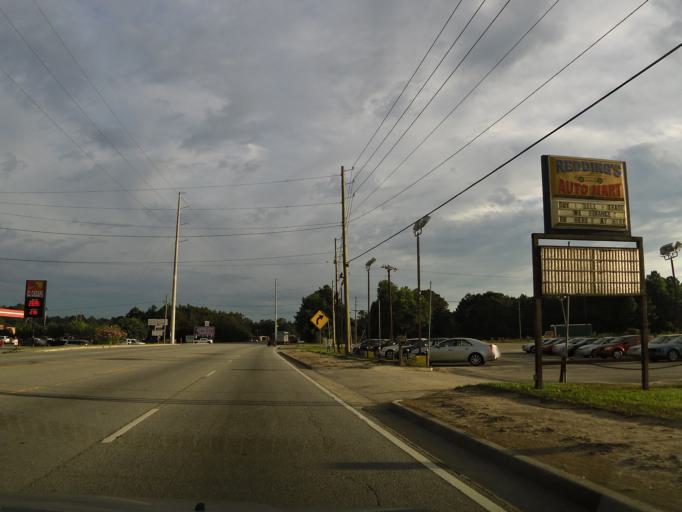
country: US
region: Georgia
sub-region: Chatham County
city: Garden City
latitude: 32.0793
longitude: -81.1958
